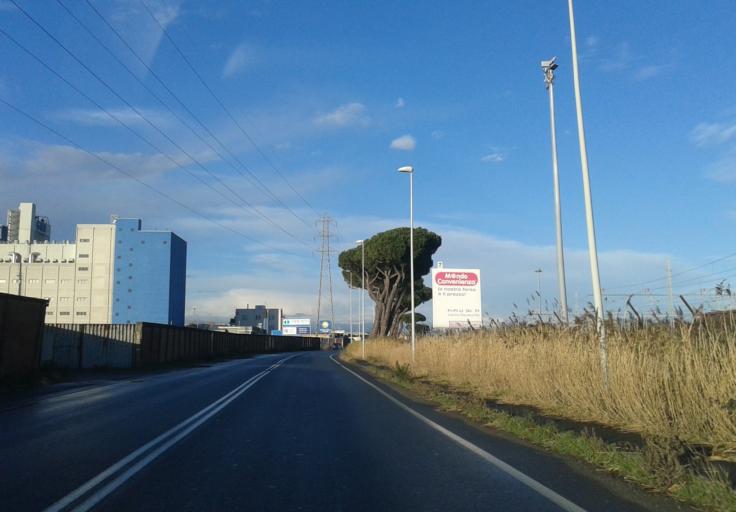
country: IT
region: Tuscany
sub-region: Provincia di Livorno
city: Livorno
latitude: 43.5764
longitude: 10.3212
